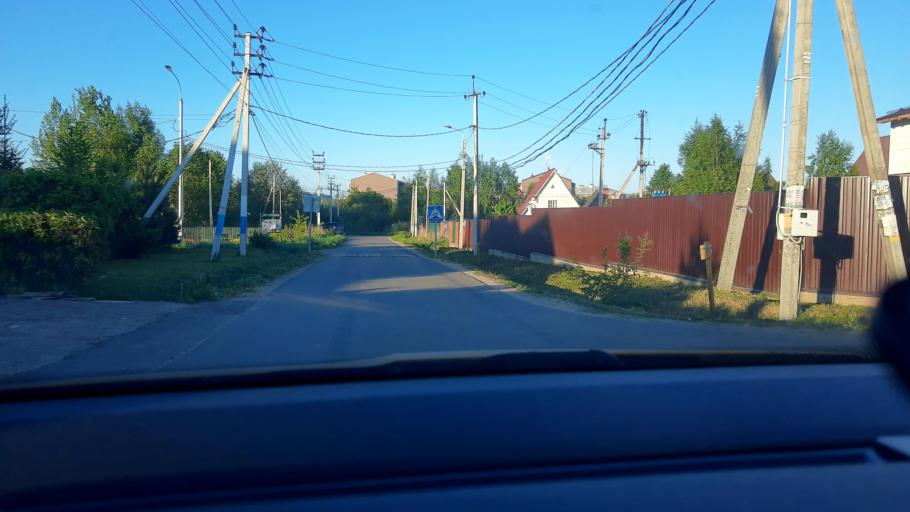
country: RU
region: Moskovskaya
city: Selyatino
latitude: 55.5010
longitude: 36.9237
